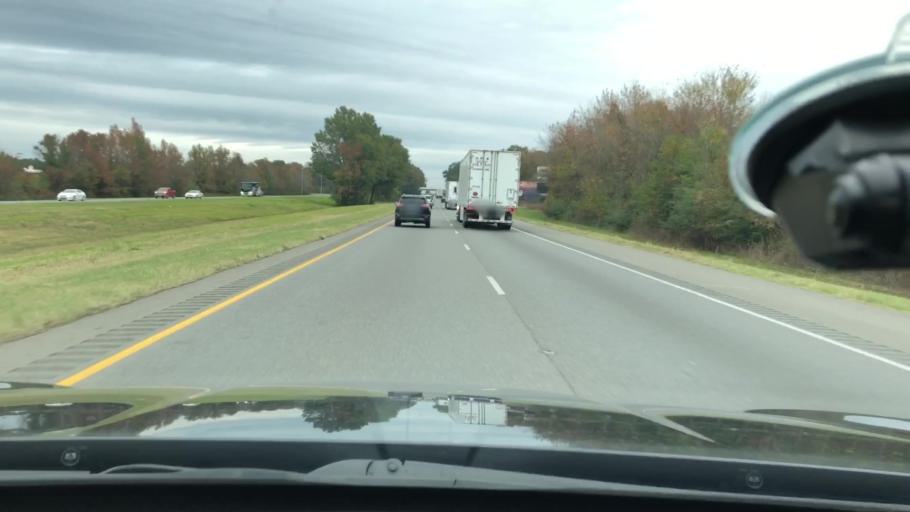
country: US
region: Arkansas
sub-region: Hempstead County
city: Hope
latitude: 33.6773
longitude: -93.6167
